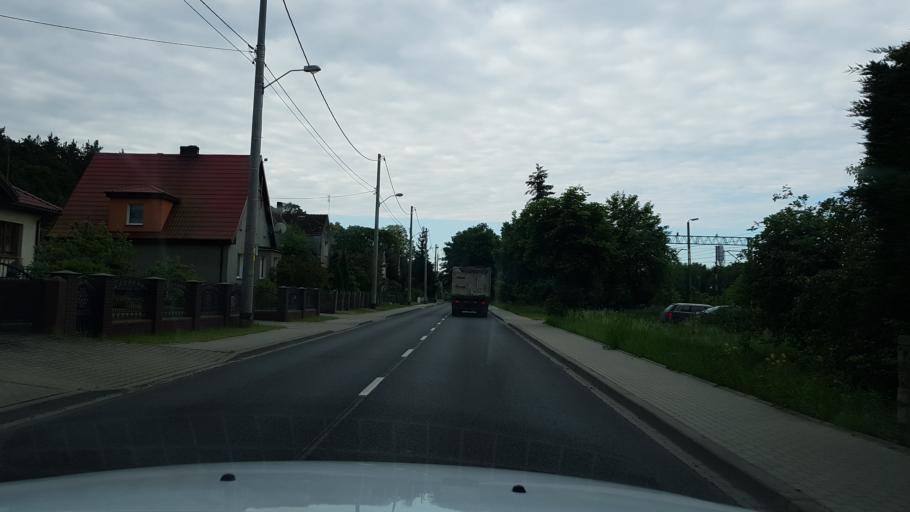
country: PL
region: West Pomeranian Voivodeship
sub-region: Powiat gryfinski
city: Gryfino
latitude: 53.3087
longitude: 14.5305
